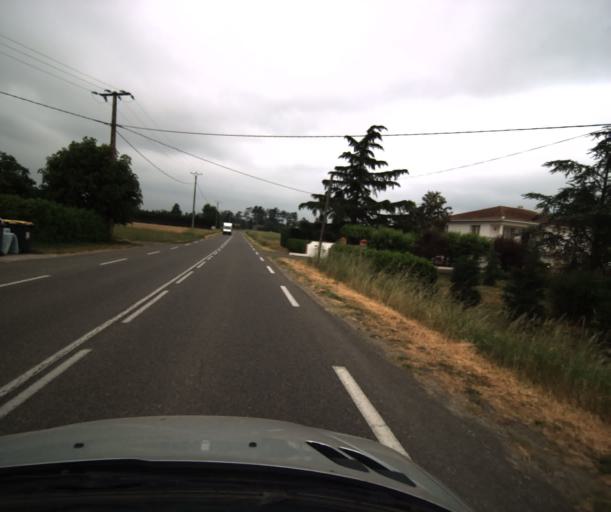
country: FR
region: Midi-Pyrenees
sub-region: Departement du Tarn-et-Garonne
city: Saint-Nicolas-de-la-Grave
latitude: 44.0412
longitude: 1.0357
